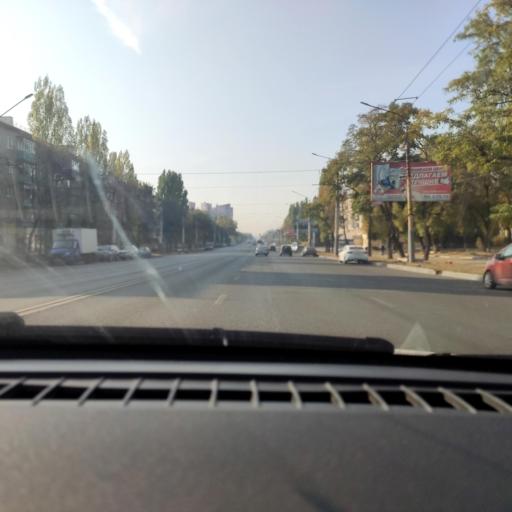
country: RU
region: Voronezj
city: Voronezh
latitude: 51.6689
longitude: 39.2508
